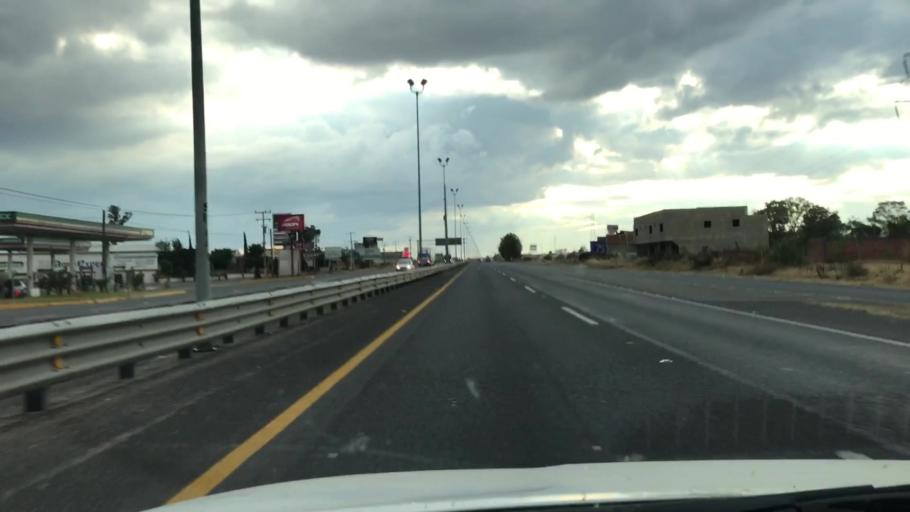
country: MX
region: Guanajuato
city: Penjamo
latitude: 20.4339
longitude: -101.7005
